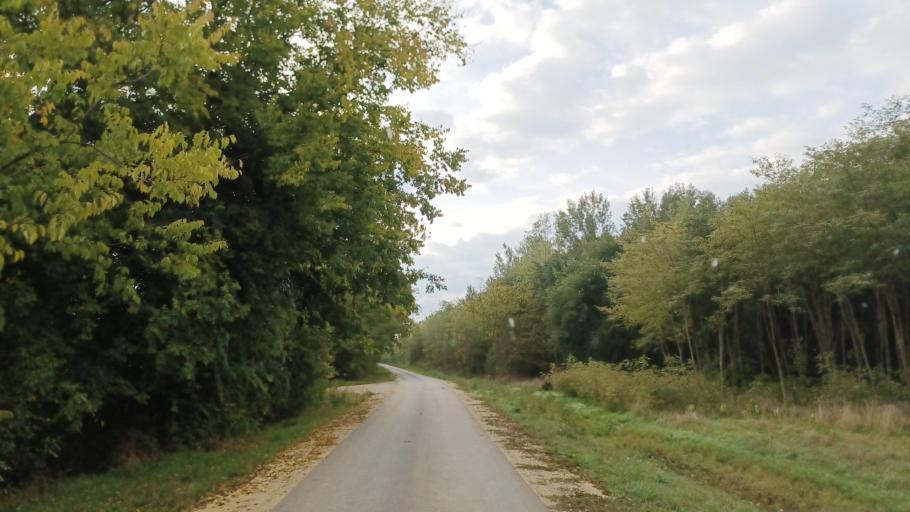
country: HU
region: Tolna
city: Tengelic
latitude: 46.5799
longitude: 18.7255
